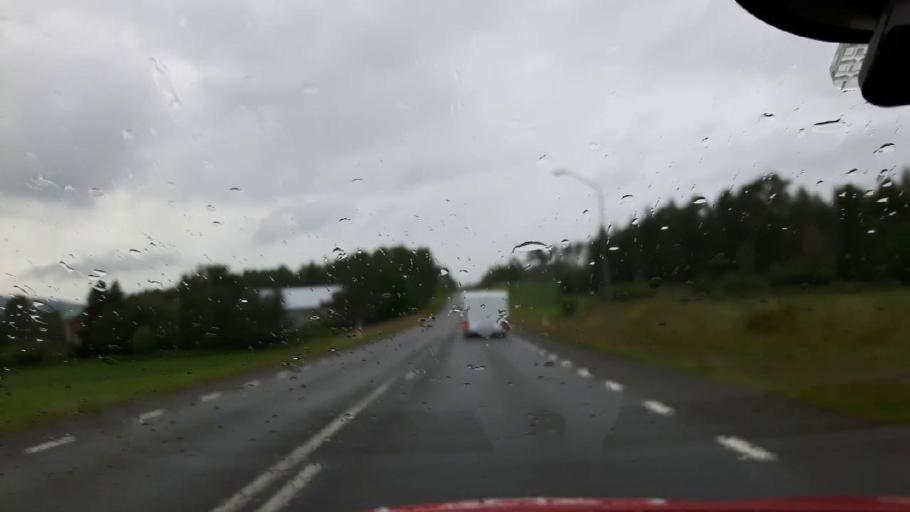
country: SE
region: Jaemtland
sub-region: Are Kommun
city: Jarpen
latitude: 63.3162
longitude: 13.5851
